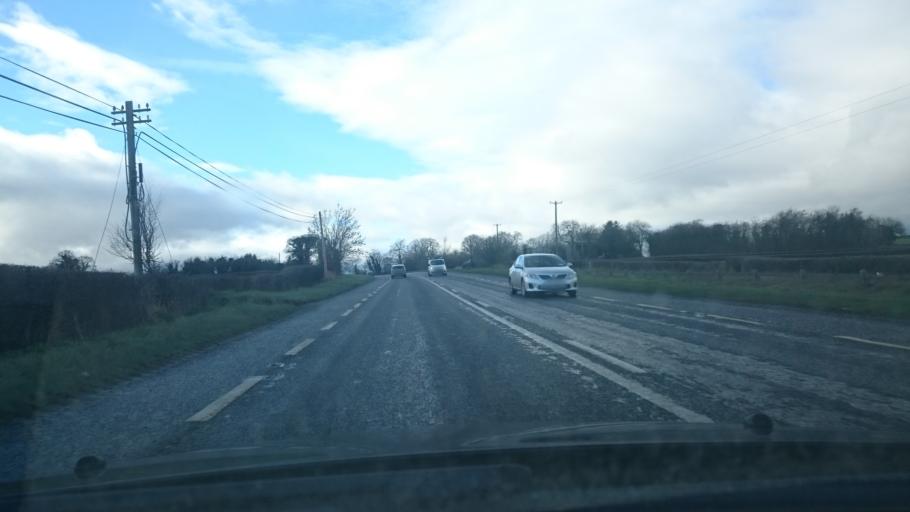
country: IE
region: Leinster
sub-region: Kilkenny
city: Callan
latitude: 52.5635
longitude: -7.3605
